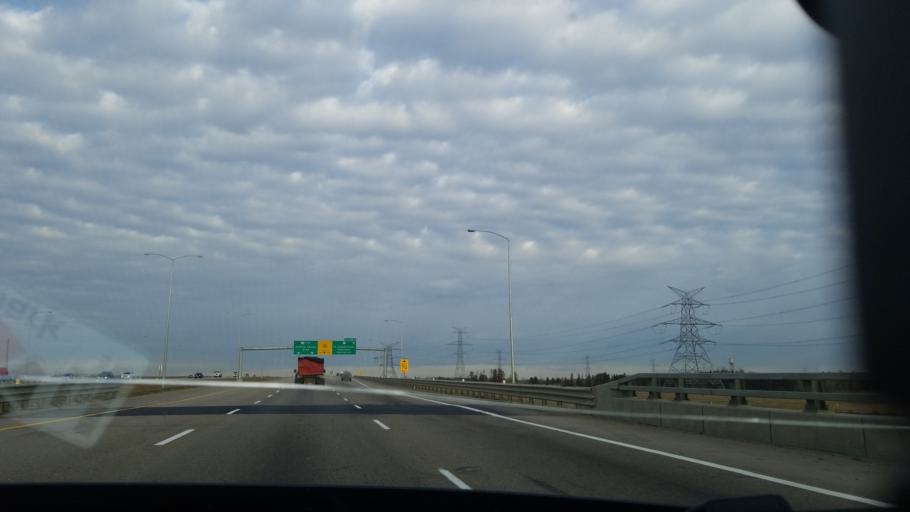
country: CA
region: Alberta
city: Sherwood Park
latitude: 53.6260
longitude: -113.3726
